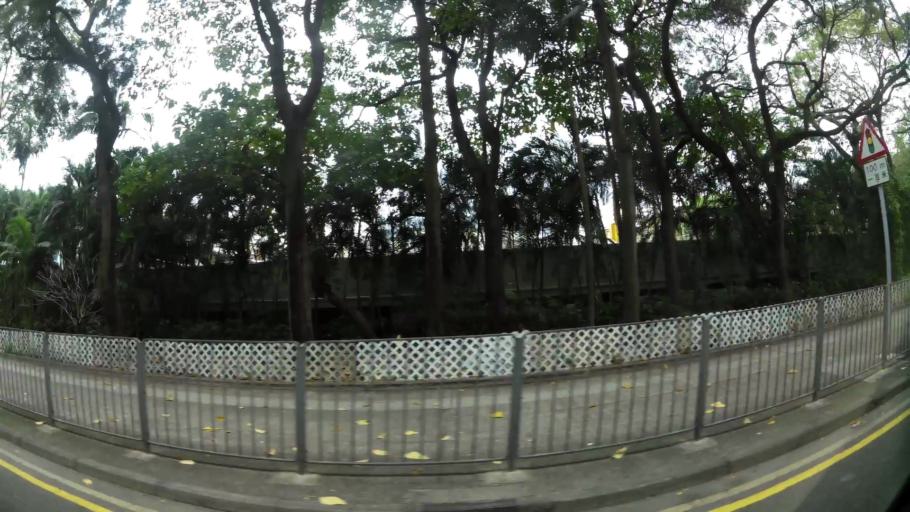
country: HK
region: Sham Shui Po
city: Sham Shui Po
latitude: 22.3306
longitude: 114.1550
